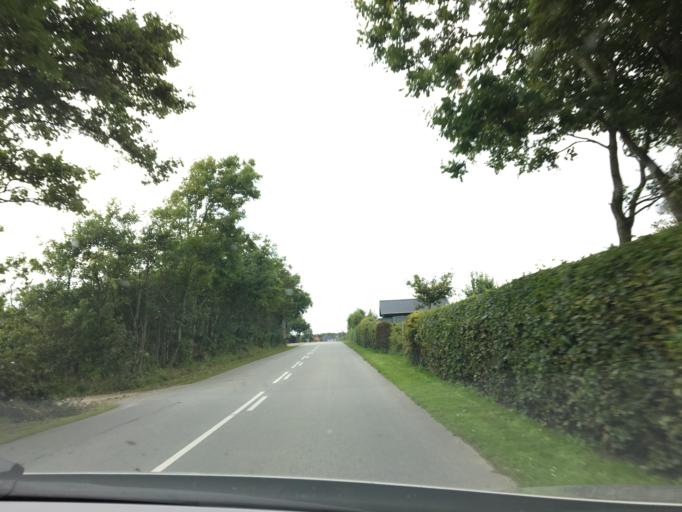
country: DK
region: South Denmark
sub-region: Varde Kommune
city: Oksbol
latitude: 55.7158
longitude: 8.3400
